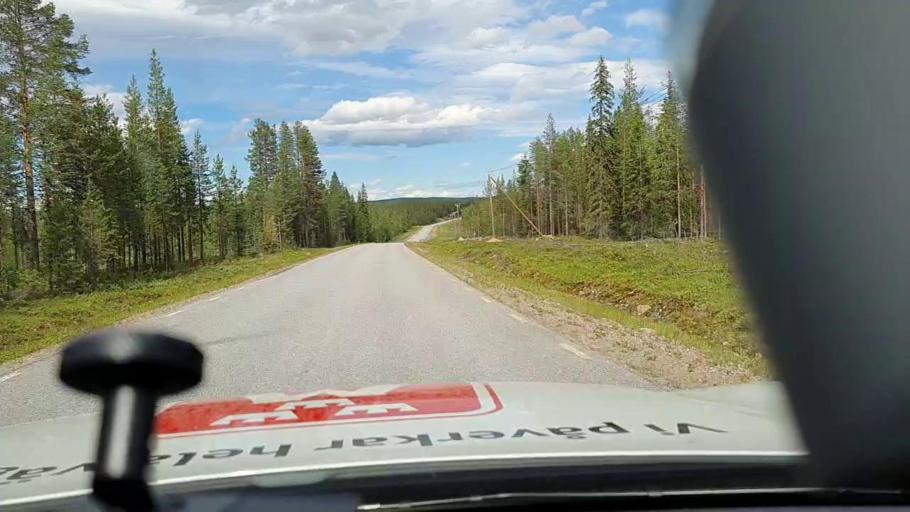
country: SE
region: Norrbotten
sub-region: Jokkmokks Kommun
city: Jokkmokk
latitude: 66.6867
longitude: 20.1679
